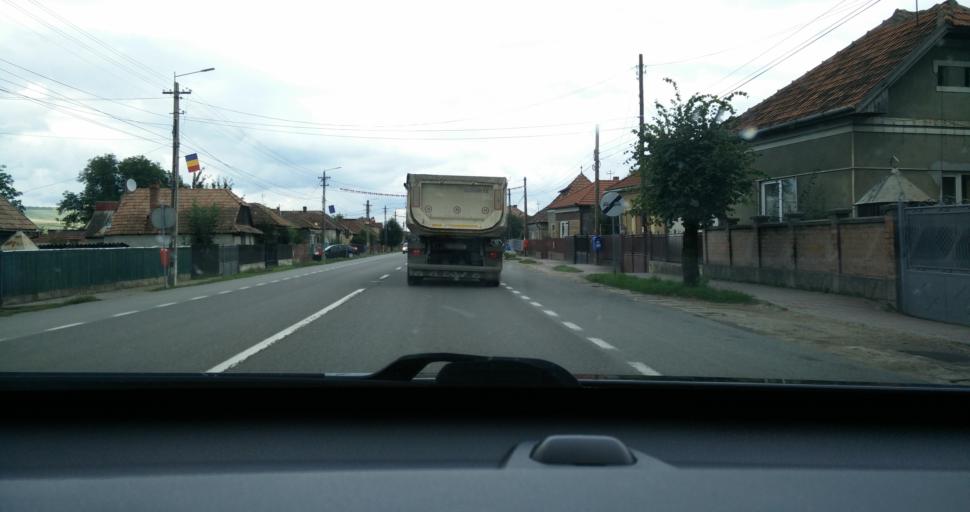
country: RO
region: Cluj
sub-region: Comuna Floresti
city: Luna de Sus
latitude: 46.7514
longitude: 23.3993
